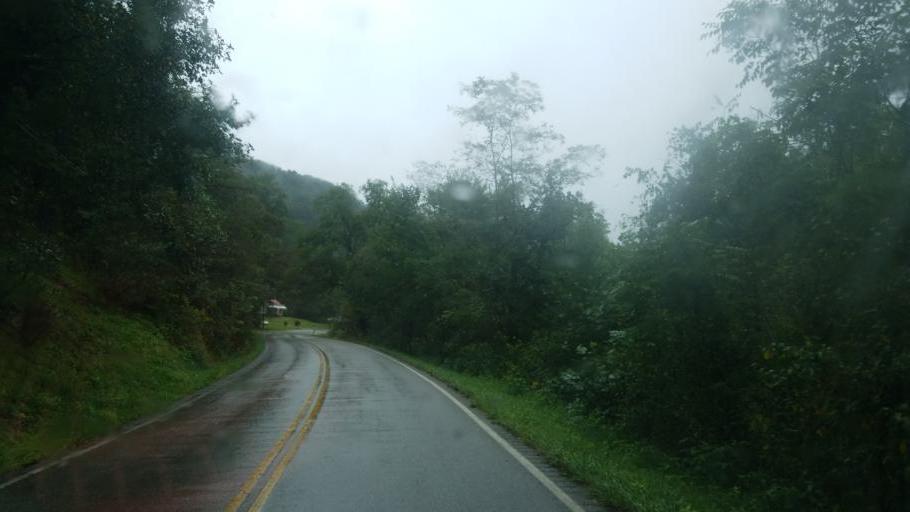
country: US
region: Kentucky
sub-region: Greenup County
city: South Shore
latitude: 38.6941
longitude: -82.9416
